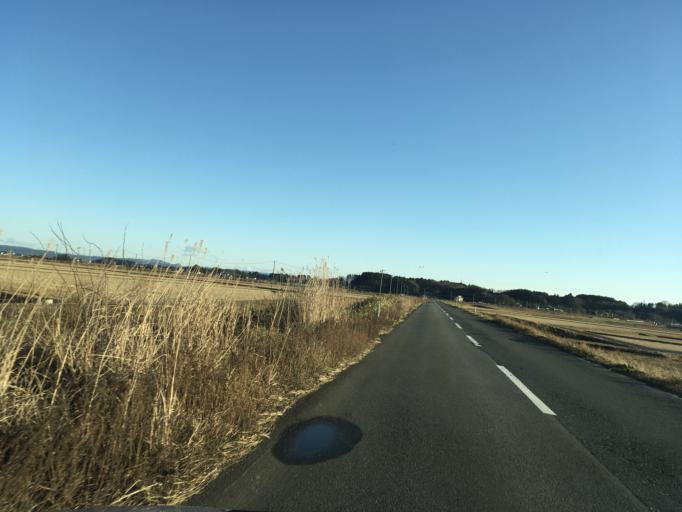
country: JP
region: Miyagi
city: Wakuya
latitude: 38.7277
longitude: 141.1269
